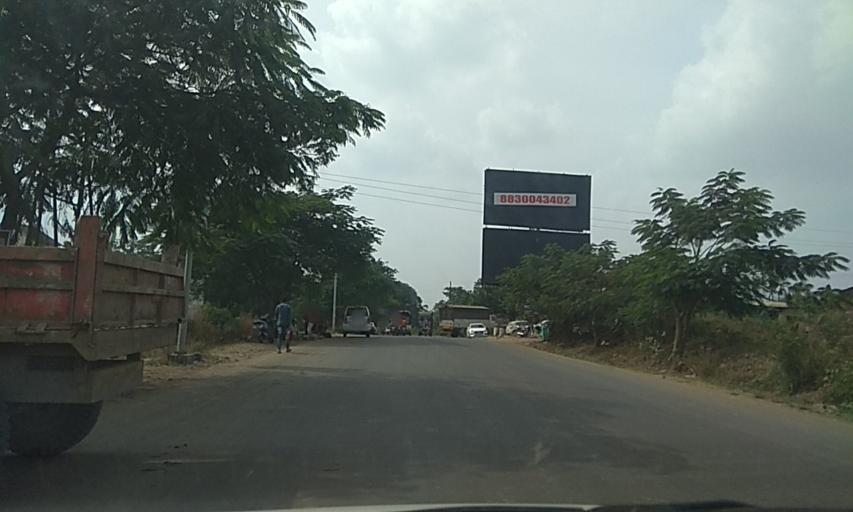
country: IN
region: Maharashtra
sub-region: Pune Division
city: Pimpri
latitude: 18.5807
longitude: 73.7212
